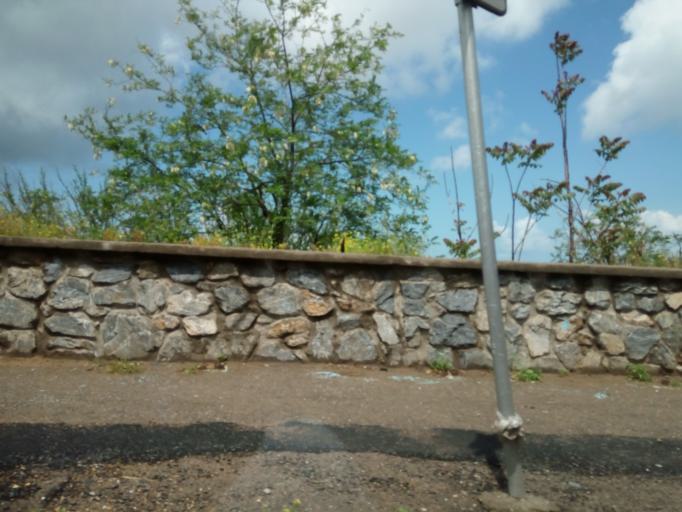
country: DZ
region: Alger
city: Algiers
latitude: 36.7761
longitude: 3.0469
